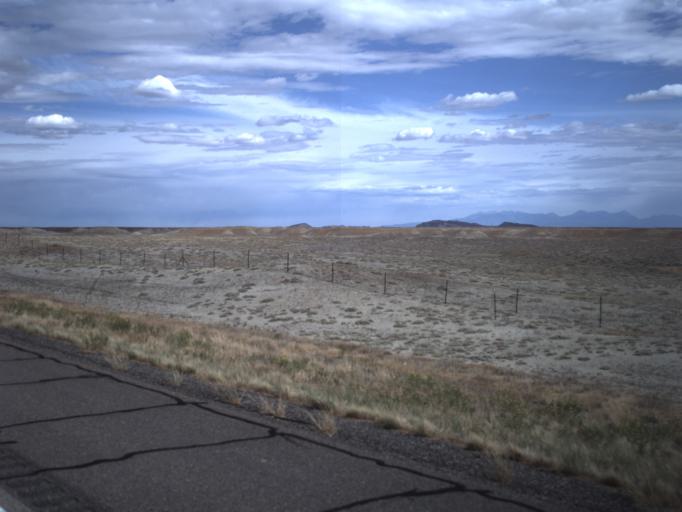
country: US
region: Utah
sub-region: Grand County
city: Moab
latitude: 38.9249
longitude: -109.9095
